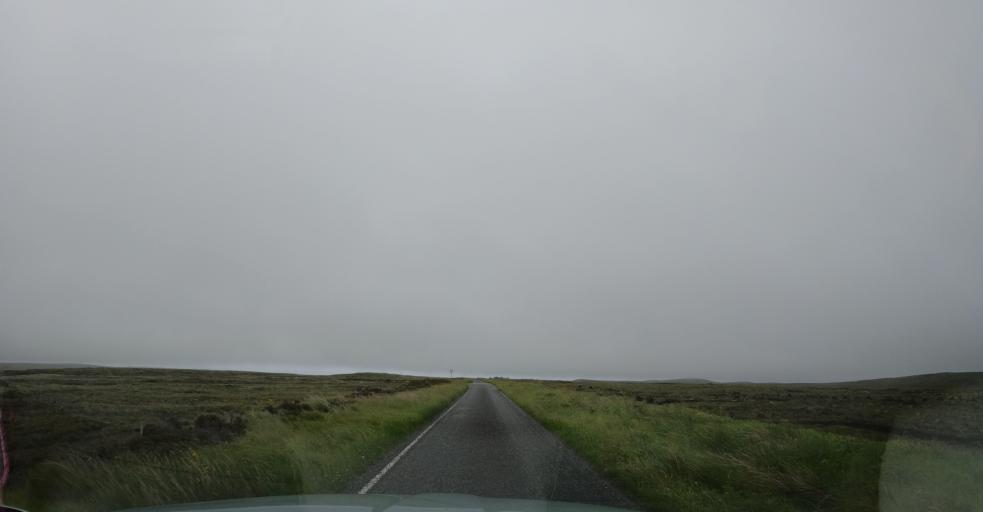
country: GB
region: Scotland
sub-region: Eilean Siar
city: Stornoway
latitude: 58.2035
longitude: -6.2421
